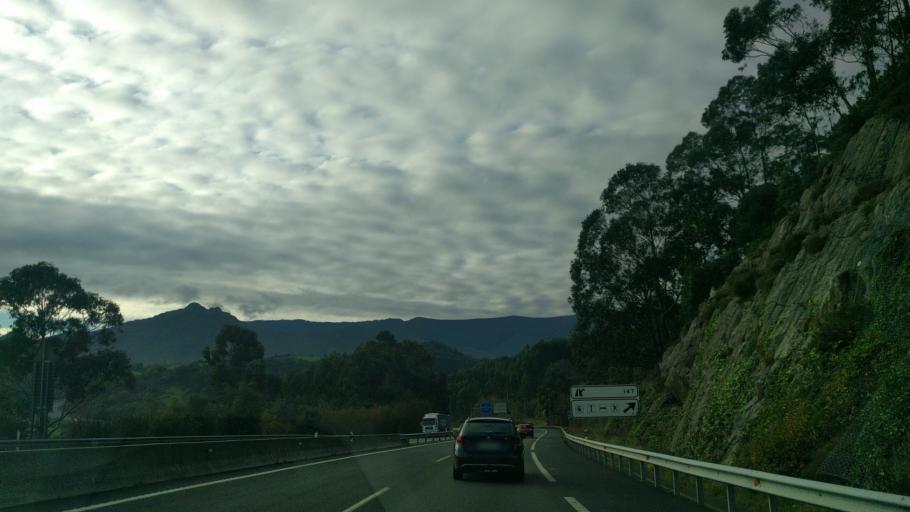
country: ES
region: Cantabria
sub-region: Provincia de Cantabria
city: Castro-Urdiales
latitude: 43.3718
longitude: -3.2194
